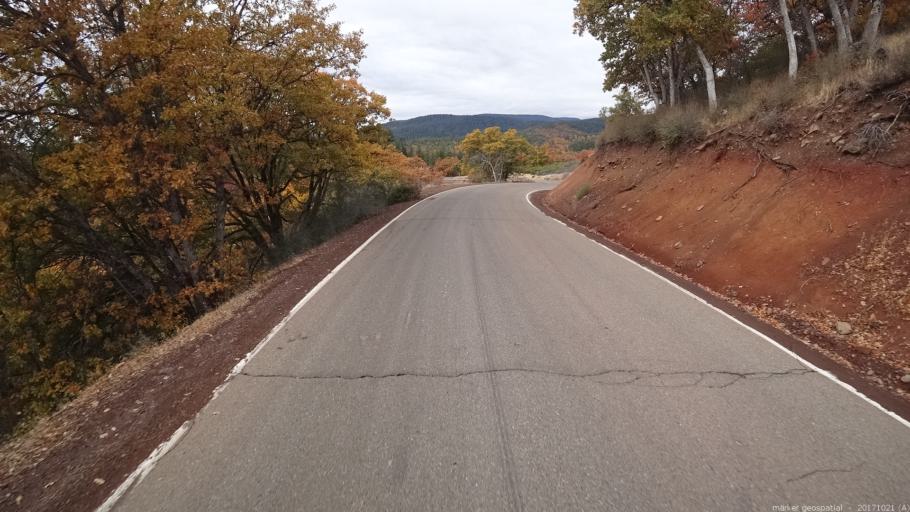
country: US
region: California
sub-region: Shasta County
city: Burney
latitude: 41.0422
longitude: -121.6630
